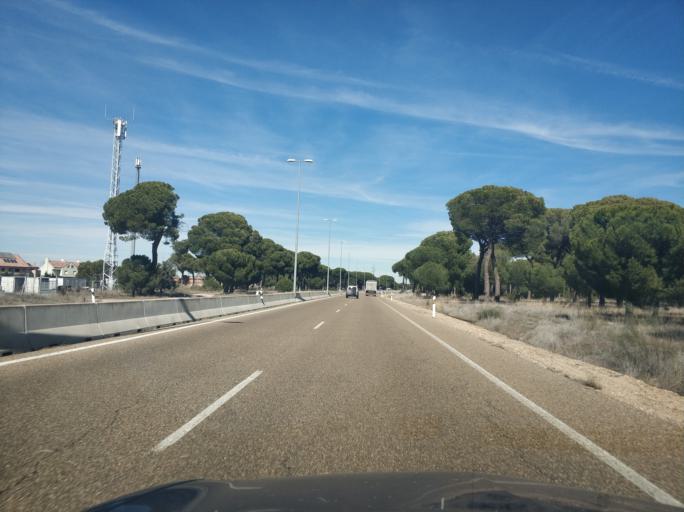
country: ES
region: Castille and Leon
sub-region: Provincia de Valladolid
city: Viana de Cega
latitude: 41.5558
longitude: -4.7873
